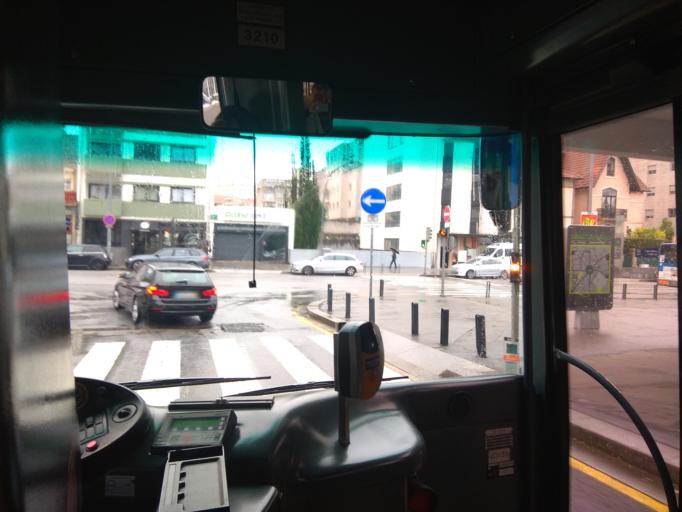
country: PT
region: Porto
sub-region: Porto
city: Porto
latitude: 41.1608
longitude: -8.6287
